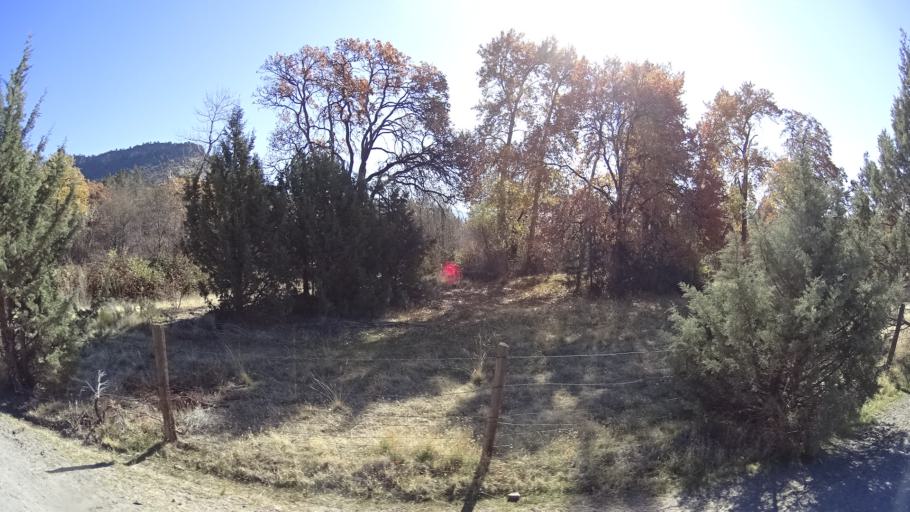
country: US
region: California
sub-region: Siskiyou County
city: Montague
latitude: 41.7331
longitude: -122.3508
